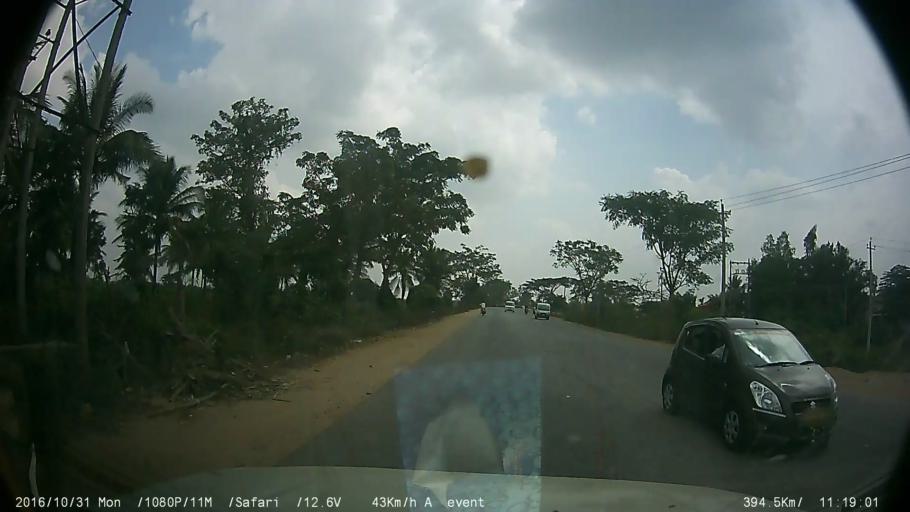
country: IN
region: Karnataka
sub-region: Mysore
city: Piriyapatna
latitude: 12.3389
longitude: 76.1436
